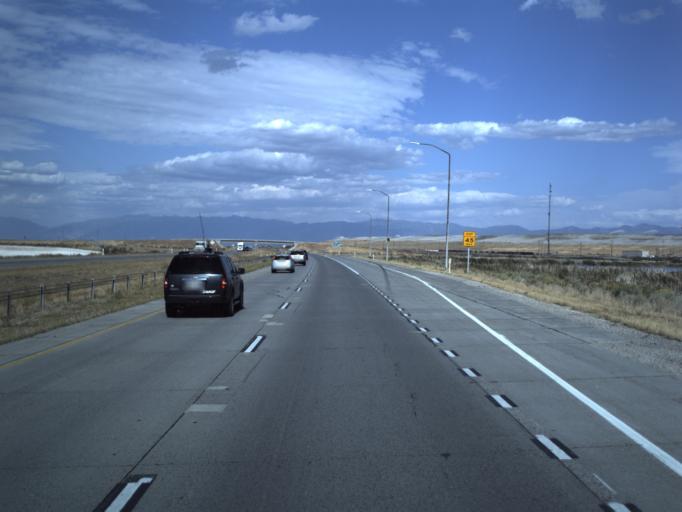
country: US
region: Utah
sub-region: Salt Lake County
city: Magna
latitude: 40.7399
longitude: -112.1898
